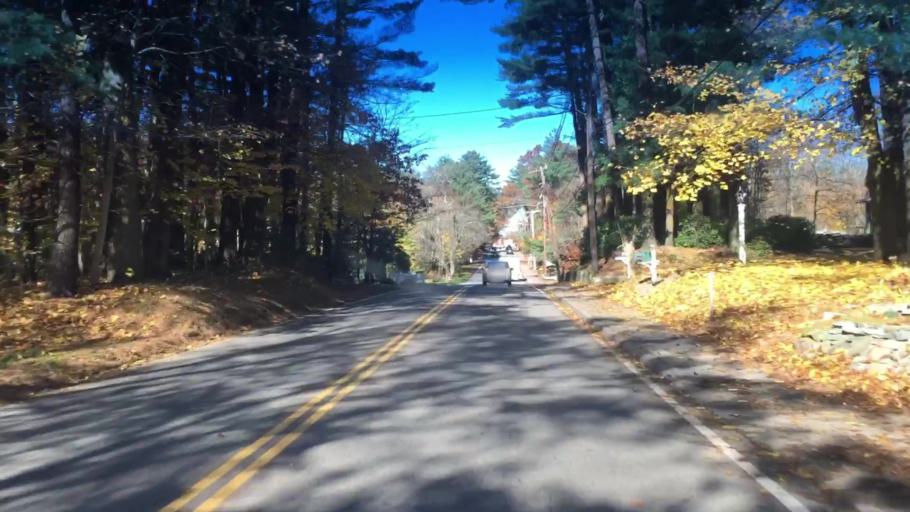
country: US
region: Massachusetts
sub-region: Norfolk County
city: Medfield
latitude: 42.1808
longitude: -71.3041
